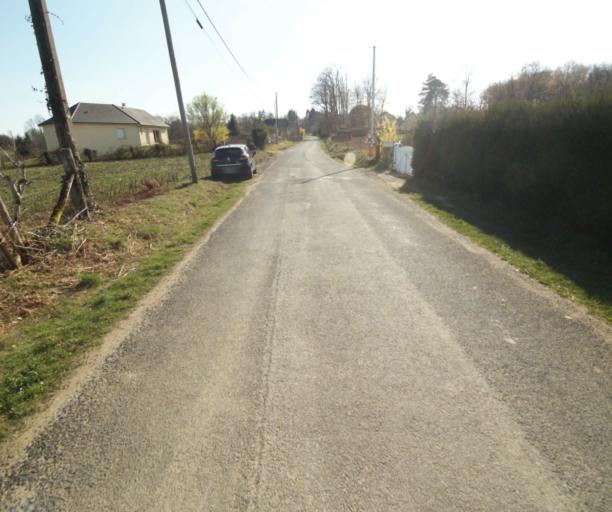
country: FR
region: Limousin
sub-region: Departement de la Correze
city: Saint-Mexant
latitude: 45.3197
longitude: 1.6231
